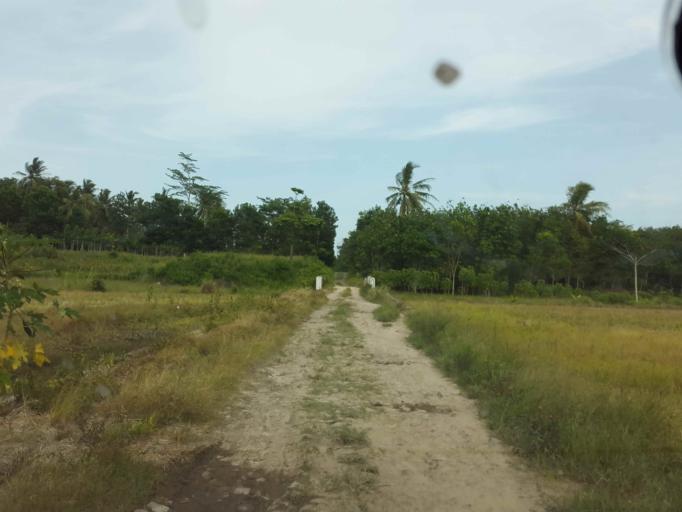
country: ID
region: Lampung
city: Sidorejo
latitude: -5.5932
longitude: 105.6055
